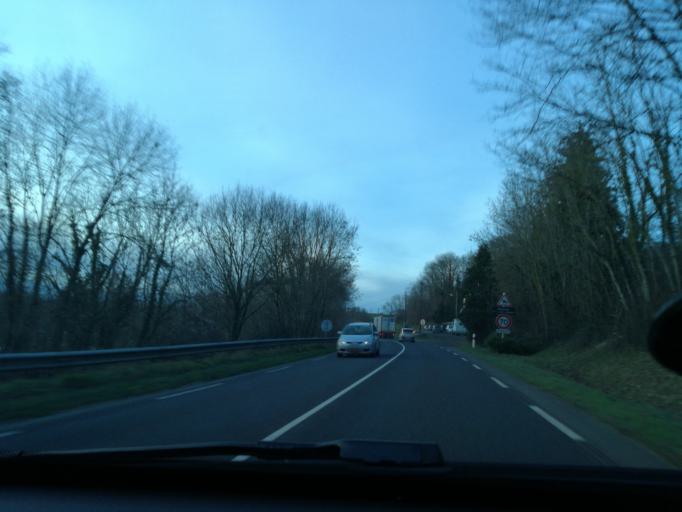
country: FR
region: Lorraine
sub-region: Departement de la Meuse
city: Fains-Veel
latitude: 48.8074
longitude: 5.1131
